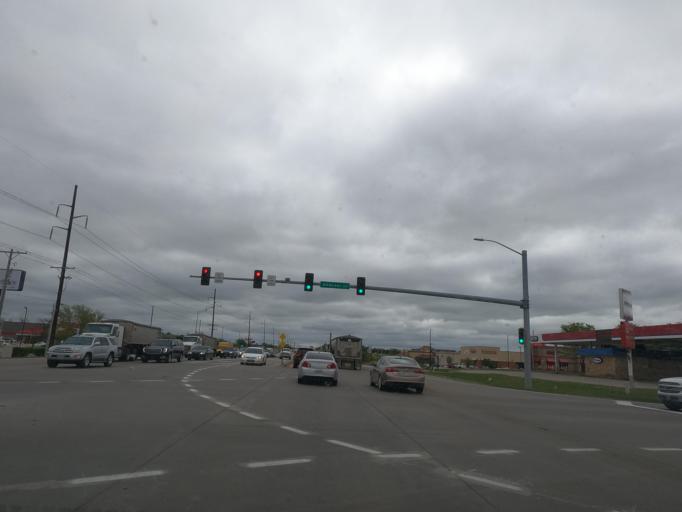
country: US
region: Kansas
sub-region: Butler County
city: Andover
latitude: 37.6796
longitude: -97.1353
